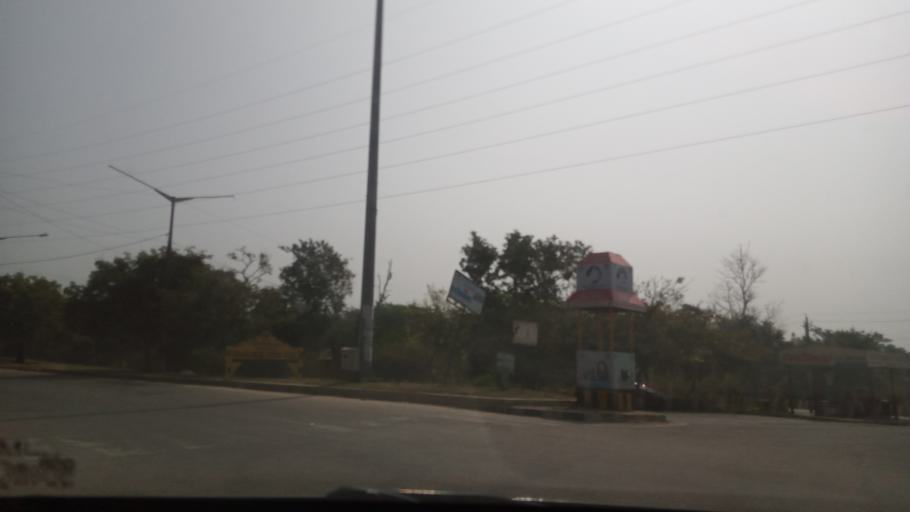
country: IN
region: Karnataka
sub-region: Mysore
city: Mysore
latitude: 12.2876
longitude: 76.6176
